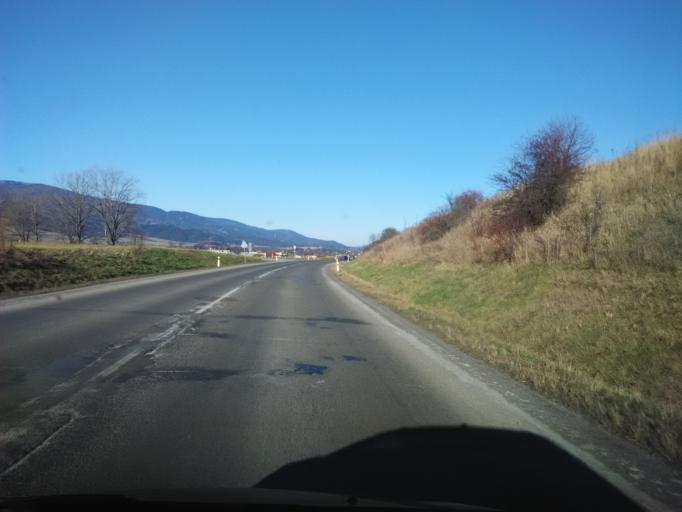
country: SK
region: Zilinsky
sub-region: Okres Martin
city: Martin
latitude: 48.9972
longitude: 18.8888
